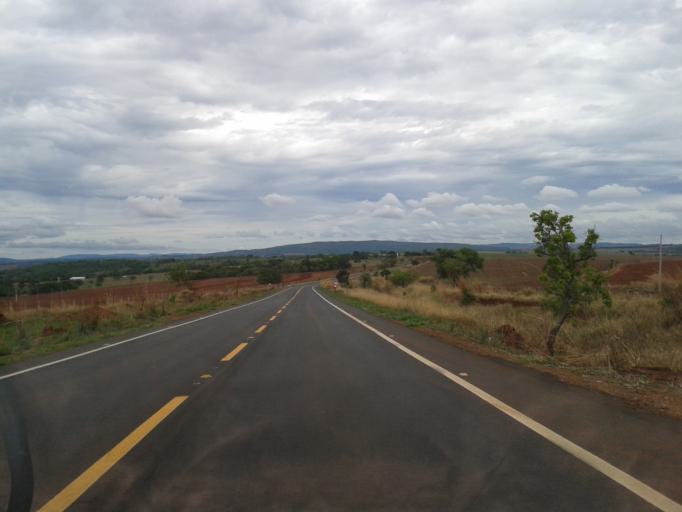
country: BR
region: Goias
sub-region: Caldas Novas
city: Caldas Novas
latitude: -17.8794
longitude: -48.6478
